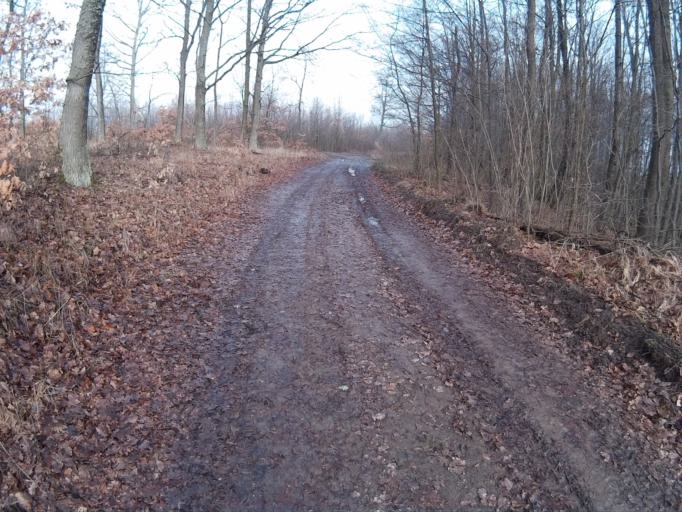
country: HU
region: Borsod-Abauj-Zemplen
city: Tolcsva
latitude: 48.3592
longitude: 21.4842
